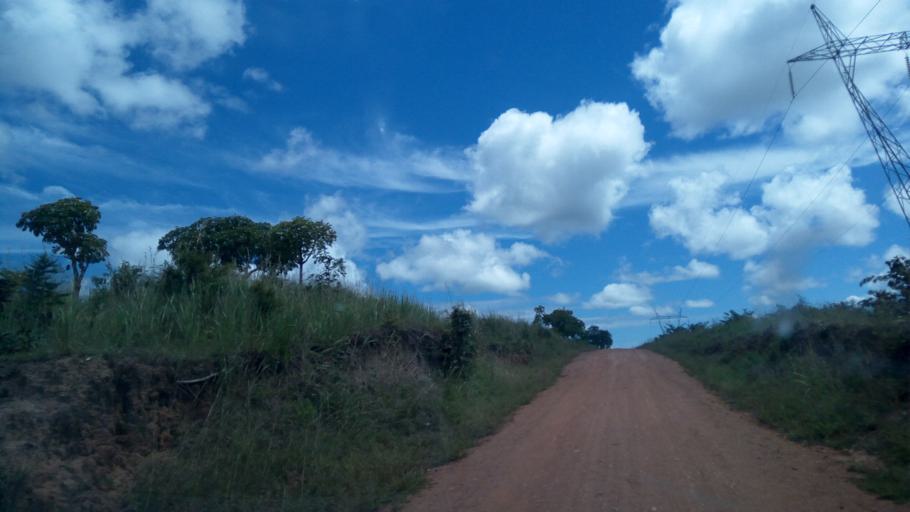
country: CD
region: Katanga
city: Kalemie
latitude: -5.7694
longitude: 29.1056
